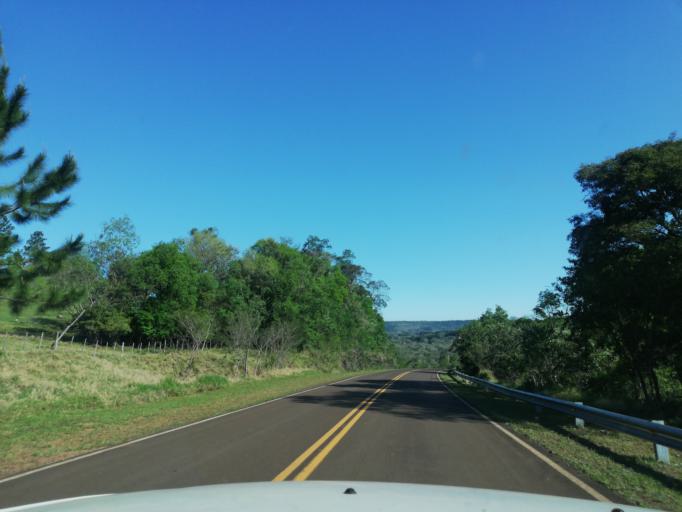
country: AR
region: Misiones
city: Arroyo del Medio
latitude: -27.6627
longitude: -55.3994
